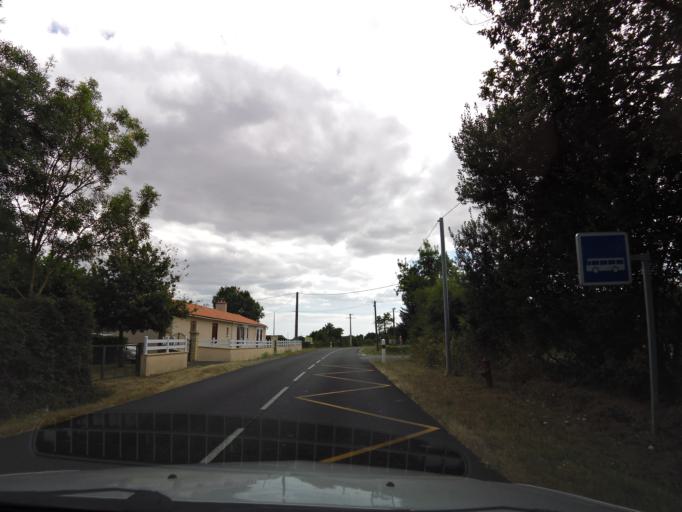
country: FR
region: Pays de la Loire
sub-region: Departement de la Vendee
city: Avrille
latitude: 46.4662
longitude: -1.4519
